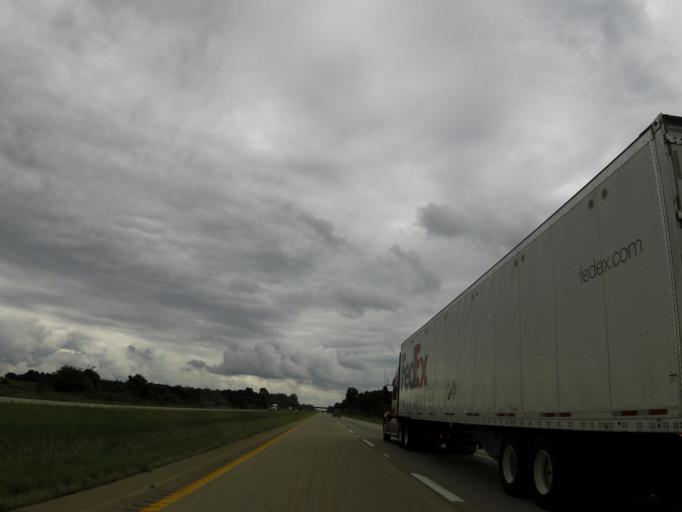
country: US
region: Missouri
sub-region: Mississippi County
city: Charleston
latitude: 36.9370
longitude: -89.2999
